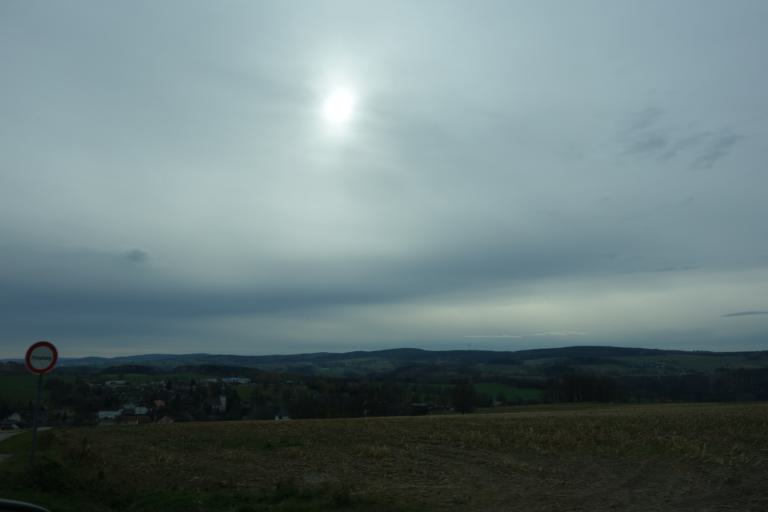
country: DE
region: Saxony
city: Leubsdorf
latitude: 50.8069
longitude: 13.1659
